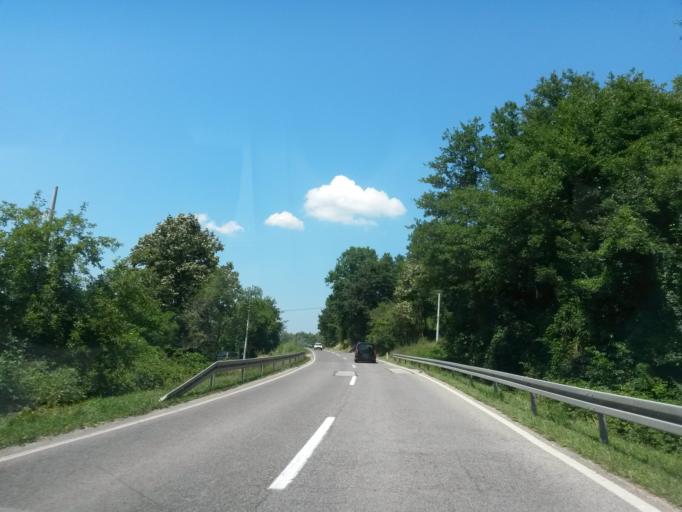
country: BA
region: Federation of Bosnia and Herzegovina
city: Lukavica
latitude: 44.9325
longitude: 18.1531
